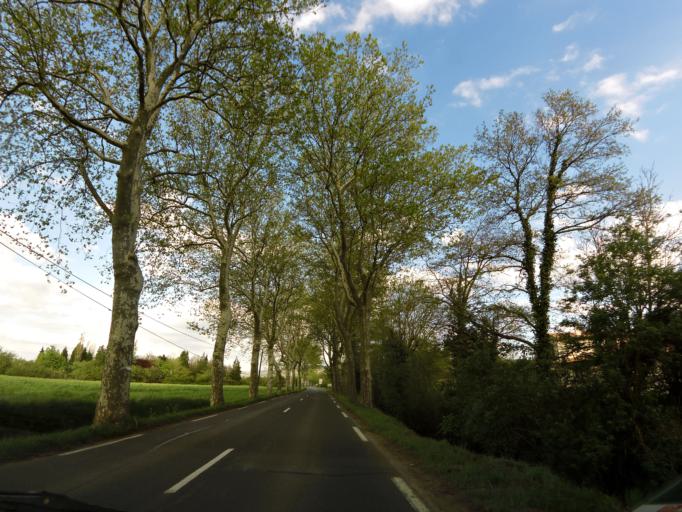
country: FR
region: Midi-Pyrenees
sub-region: Departement de la Haute-Garonne
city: Revel
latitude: 43.4532
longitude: 2.0288
